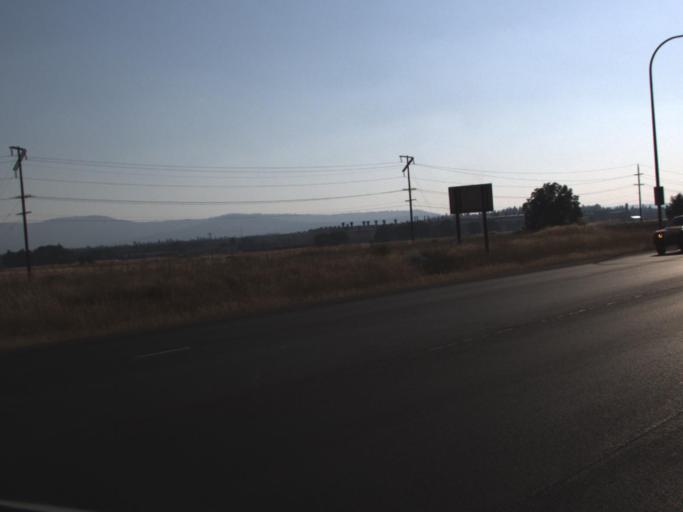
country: US
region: Washington
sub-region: Spokane County
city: Trentwood
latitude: 47.6954
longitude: -117.2013
